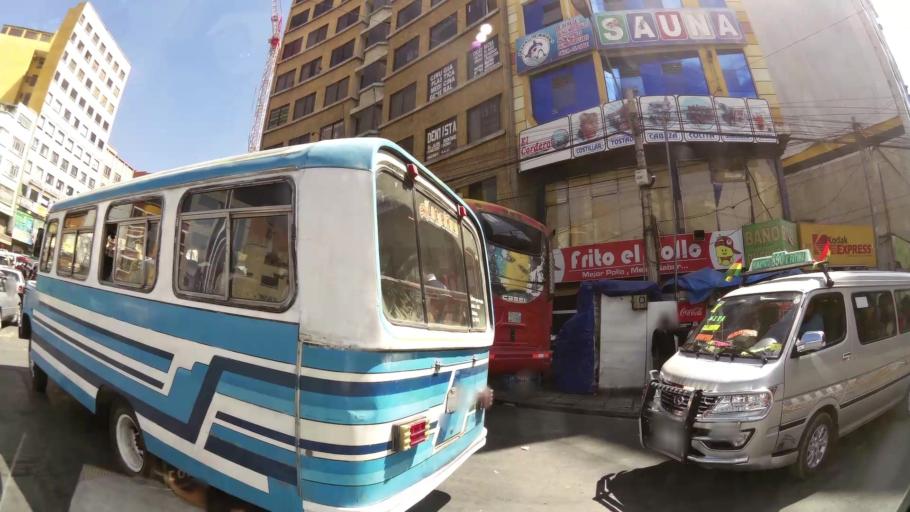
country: BO
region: La Paz
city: La Paz
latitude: -16.4937
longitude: -68.1408
